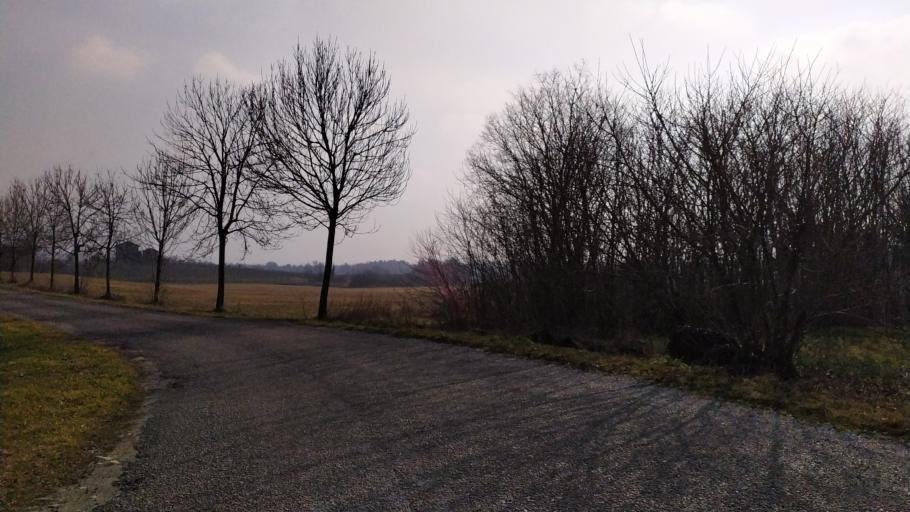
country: IT
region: Veneto
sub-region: Provincia di Treviso
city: Colle Umberto
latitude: 45.9350
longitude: 12.3473
